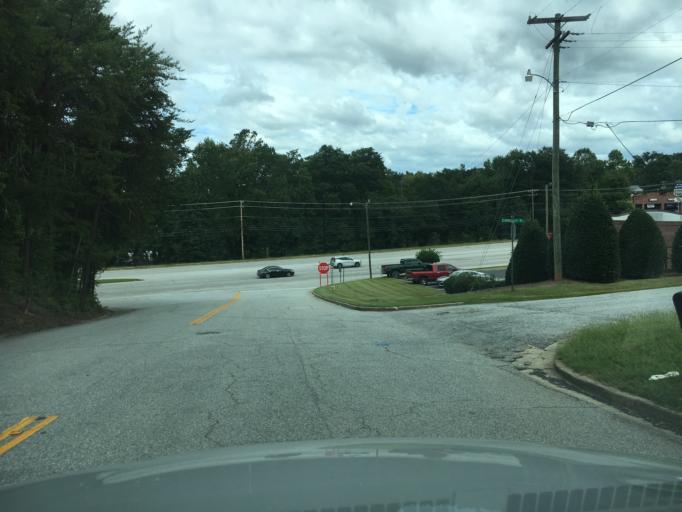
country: US
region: South Carolina
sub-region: Greenville County
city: Greer
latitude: 34.9477
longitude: -82.2302
